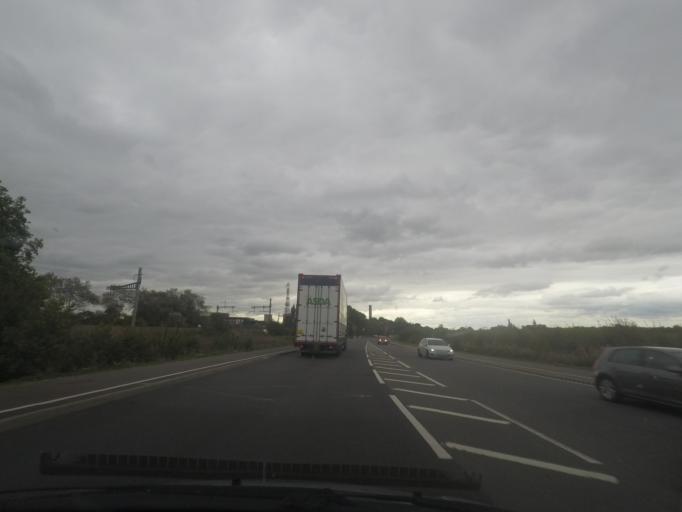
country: GB
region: England
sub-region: Oxfordshire
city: Harwell
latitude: 51.6202
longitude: -1.2964
